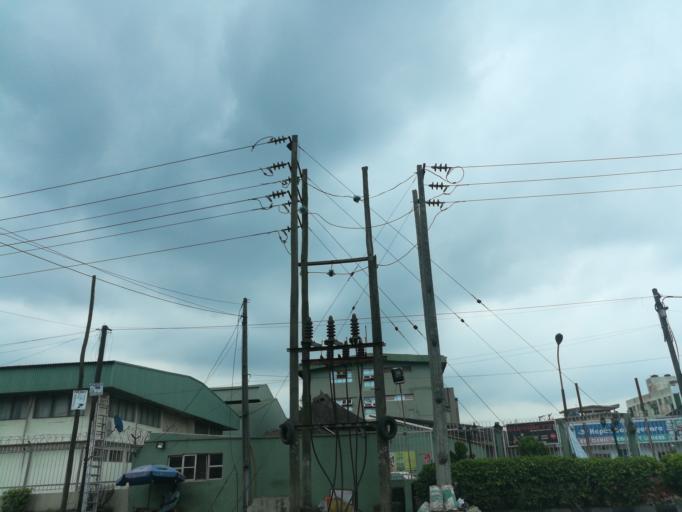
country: NG
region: Lagos
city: Ikeja
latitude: 6.6018
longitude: 3.3382
